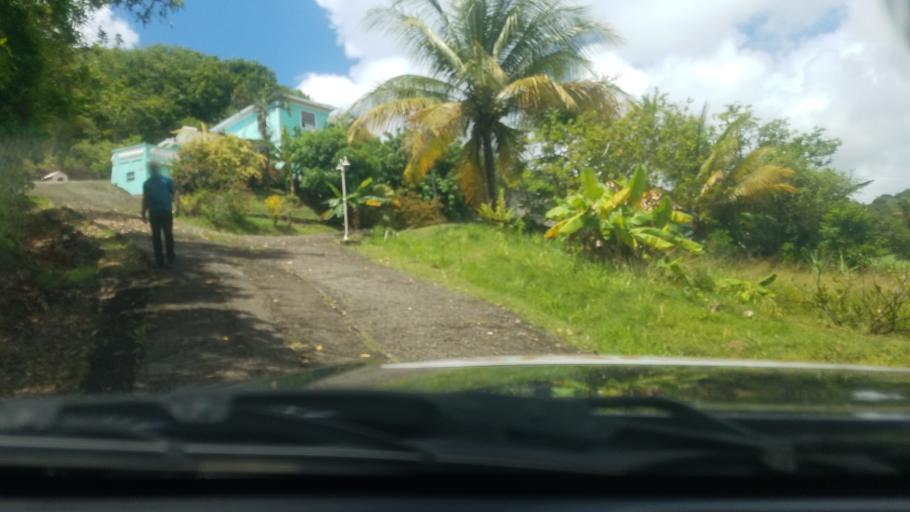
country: LC
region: Praslin
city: Praslin
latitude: 13.8746
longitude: -60.9006
